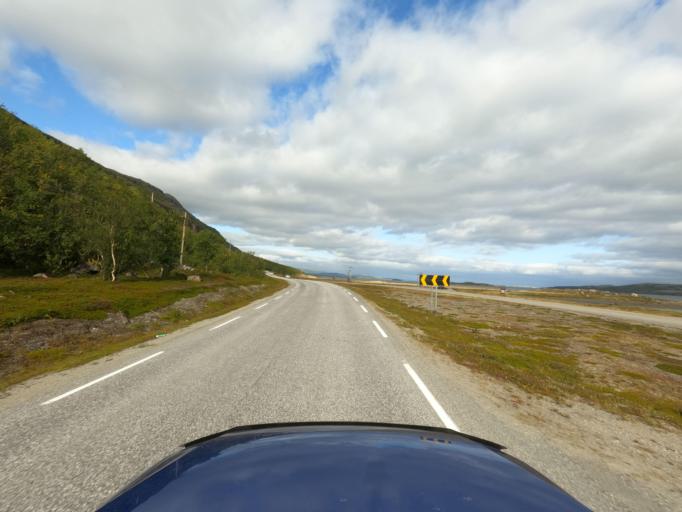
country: NO
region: Finnmark Fylke
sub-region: Porsanger
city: Lakselv
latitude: 70.1118
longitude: 24.9198
